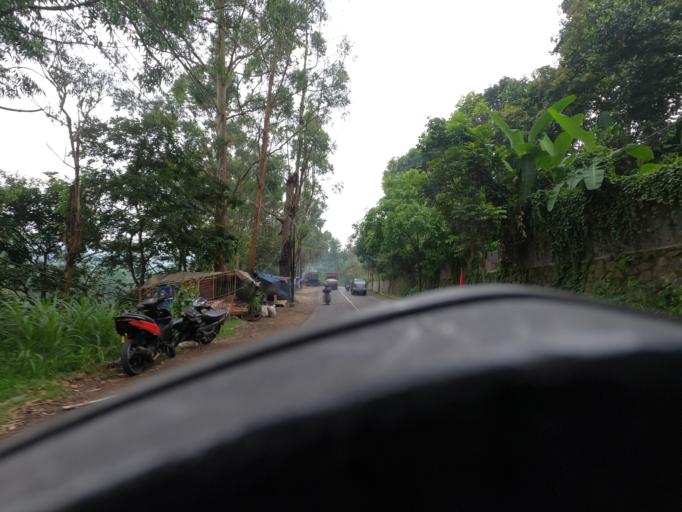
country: ID
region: West Java
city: Lembang
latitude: -6.8002
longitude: 107.5775
